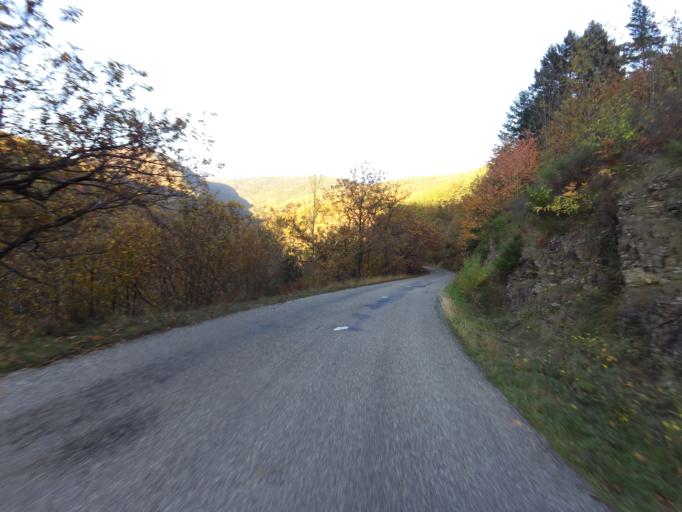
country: FR
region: Rhone-Alpes
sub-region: Departement de l'Ardeche
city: Les Vans
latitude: 44.5320
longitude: 4.0786
